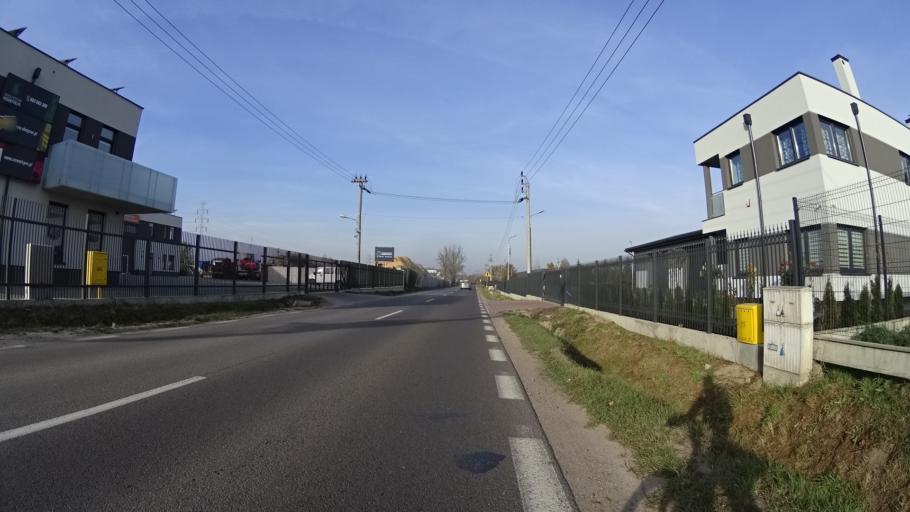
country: PL
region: Masovian Voivodeship
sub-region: Powiat warszawski zachodni
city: Babice
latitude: 52.2801
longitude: 20.8667
